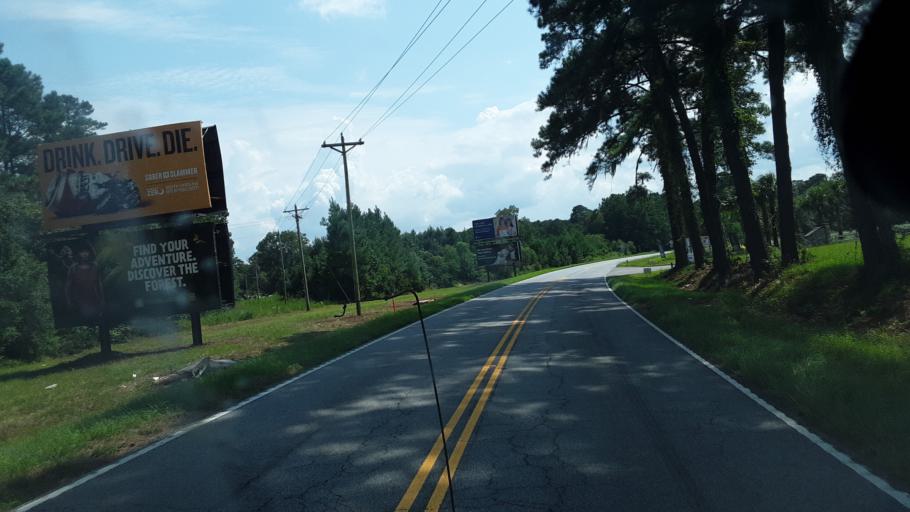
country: US
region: Georgia
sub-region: Chatham County
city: Savannah
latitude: 32.1790
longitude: -81.0278
